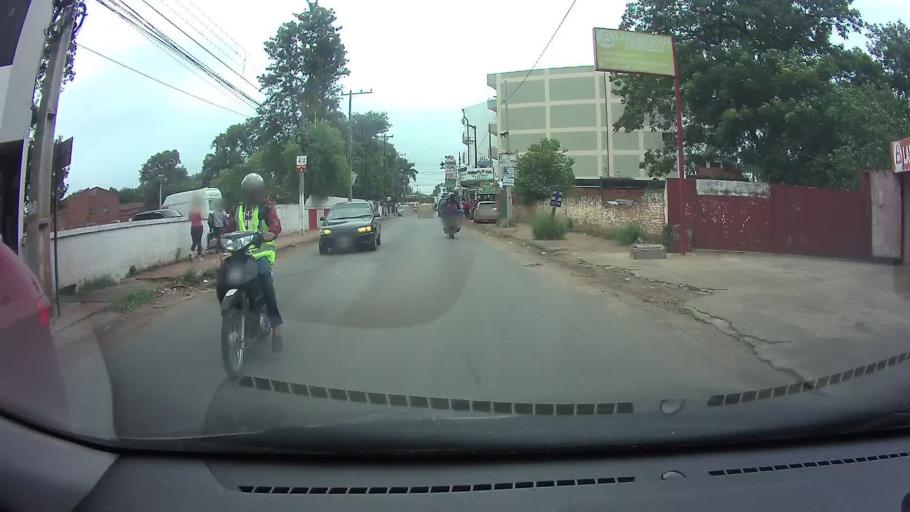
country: PY
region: Central
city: San Lorenzo
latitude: -25.3361
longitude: -57.5088
